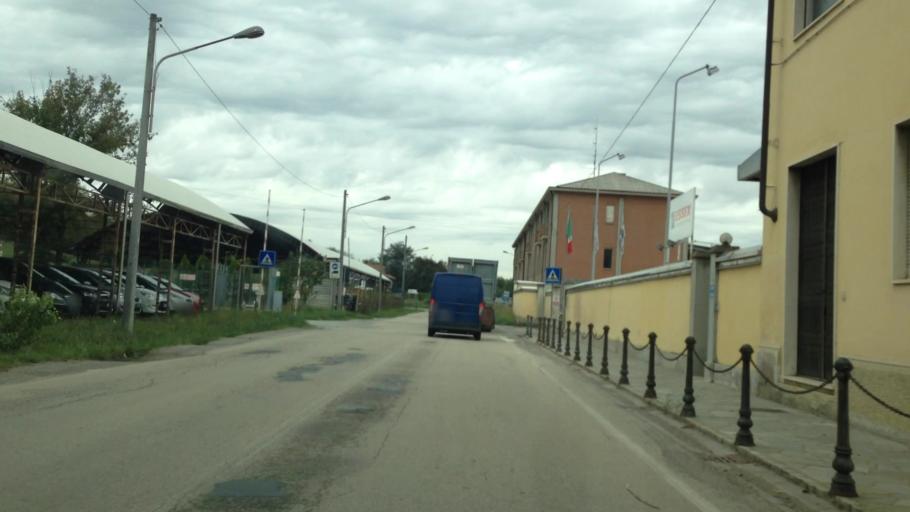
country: IT
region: Piedmont
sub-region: Provincia di Alessandria
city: Quattordio
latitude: 44.9022
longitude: 8.4056
